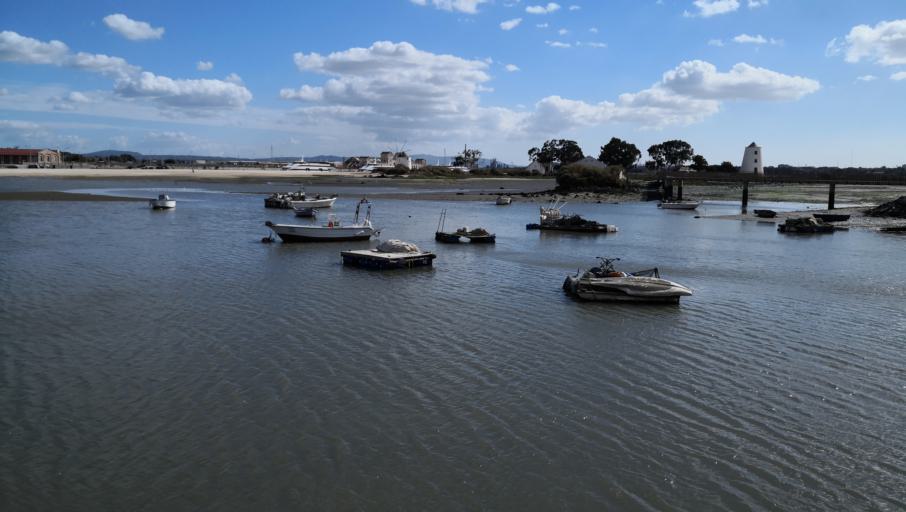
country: PT
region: Setubal
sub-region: Barreiro
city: Barreiro
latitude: 38.6581
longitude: -9.0833
